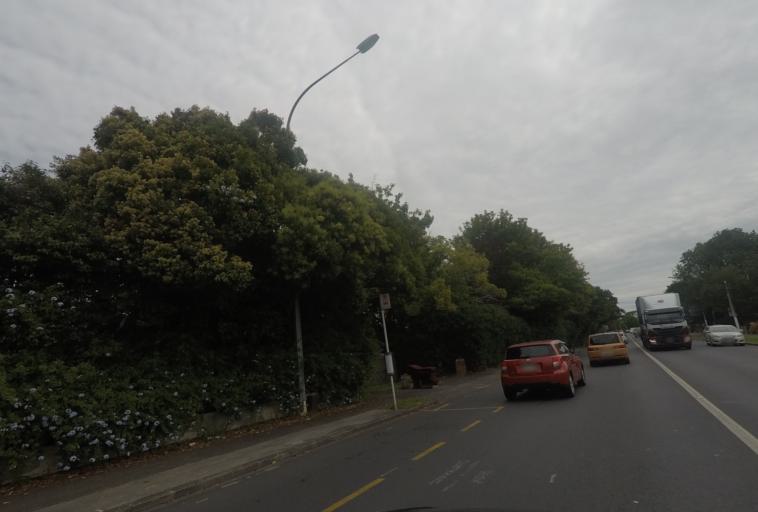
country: NZ
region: Auckland
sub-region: Auckland
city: Mangere
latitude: -36.9513
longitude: 174.8433
